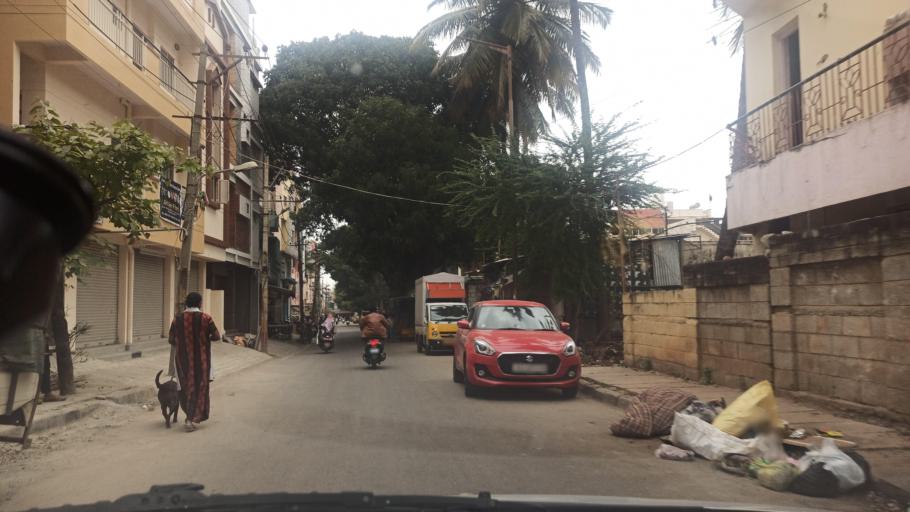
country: IN
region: Karnataka
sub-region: Bangalore Urban
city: Yelahanka
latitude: 13.0395
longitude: 77.6071
